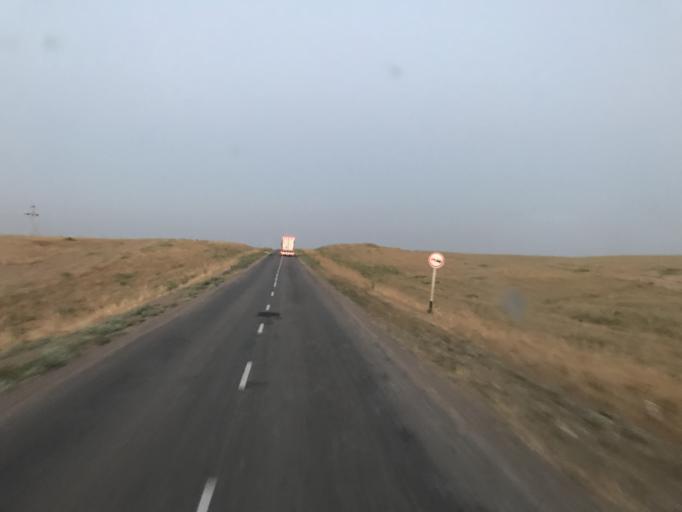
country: UZ
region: Toshkent
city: Chinoz
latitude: 41.1598
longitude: 68.6599
